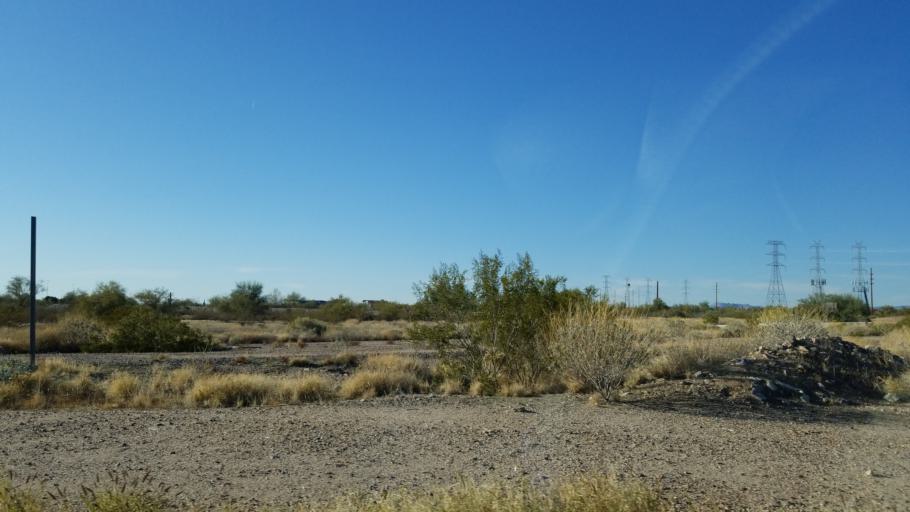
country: US
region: Arizona
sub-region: Maricopa County
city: Paradise Valley
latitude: 33.6483
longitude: -111.8905
